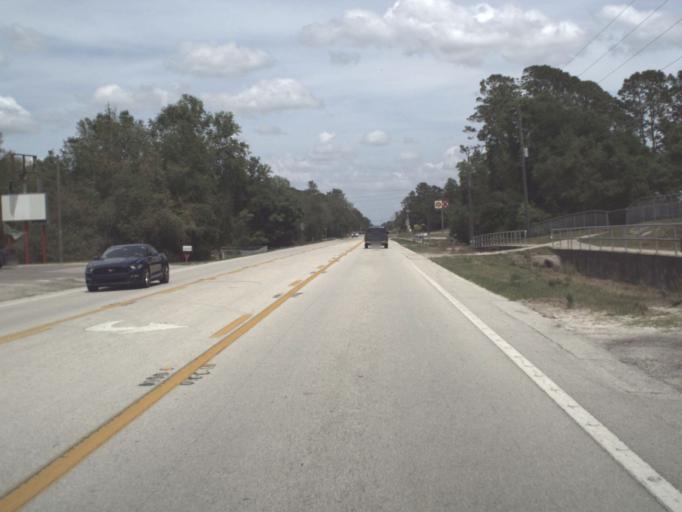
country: US
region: Florida
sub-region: Lake County
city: Lake Mack-Forest Hills
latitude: 28.9397
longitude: -81.4314
